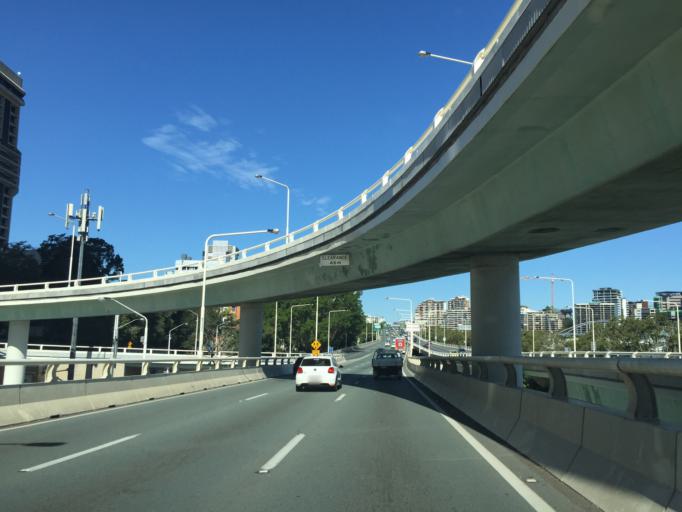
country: AU
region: Queensland
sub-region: Brisbane
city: South Brisbane
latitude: -27.4754
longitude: 153.0252
